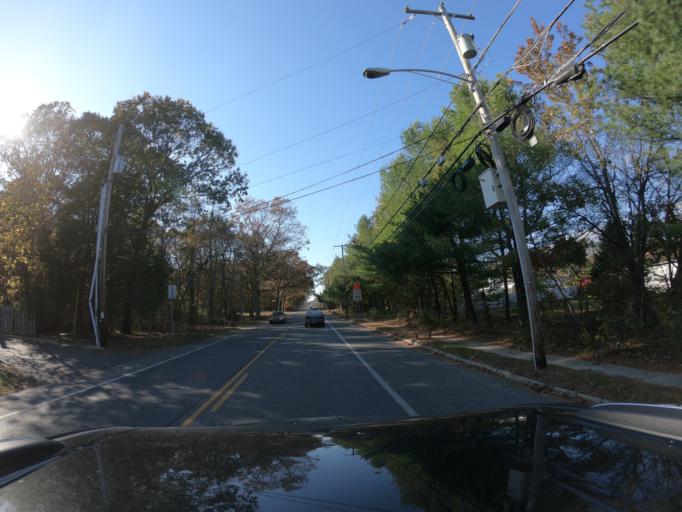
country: US
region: New Jersey
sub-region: Ocean County
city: Lakewood
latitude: 40.1049
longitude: -74.1826
